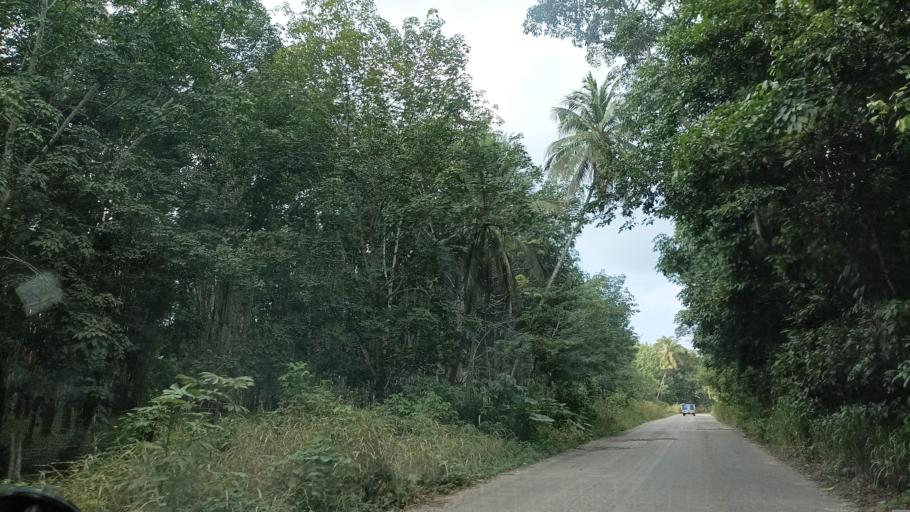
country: MX
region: Veracruz
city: Las Choapas
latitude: 17.7734
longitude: -94.1090
